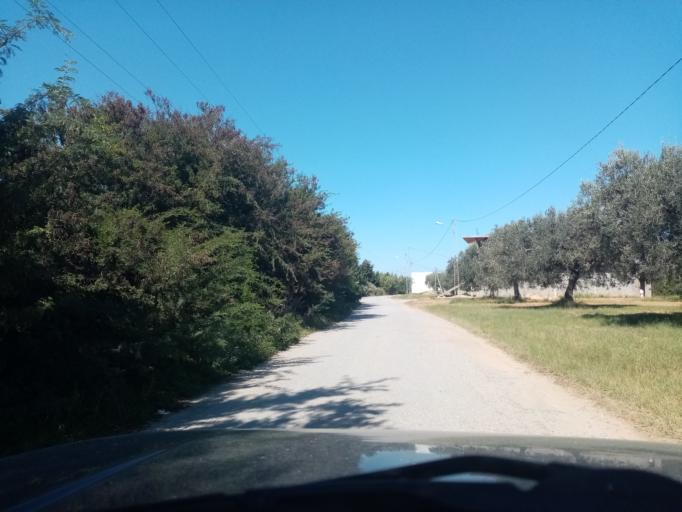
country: TN
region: Nabul
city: Bu `Urqub
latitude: 36.5689
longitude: 10.5783
